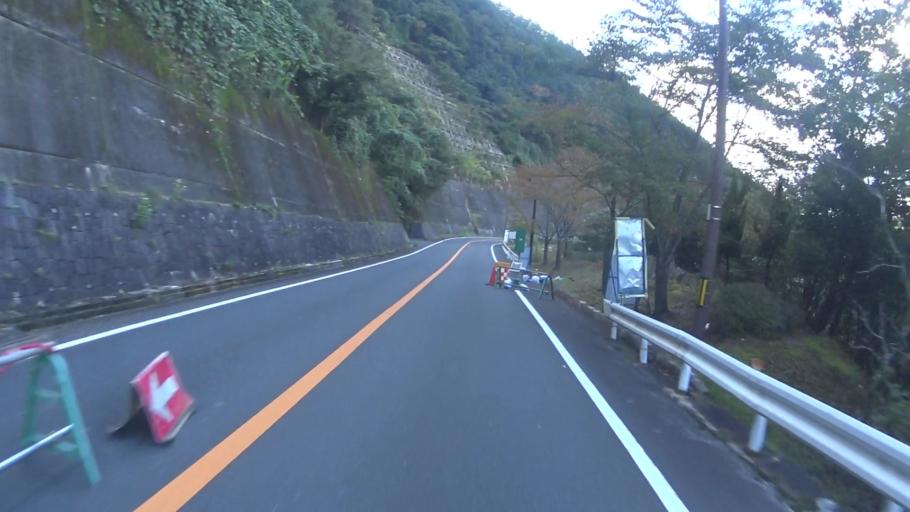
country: JP
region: Kyoto
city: Kameoka
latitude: 35.1462
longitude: 135.5167
